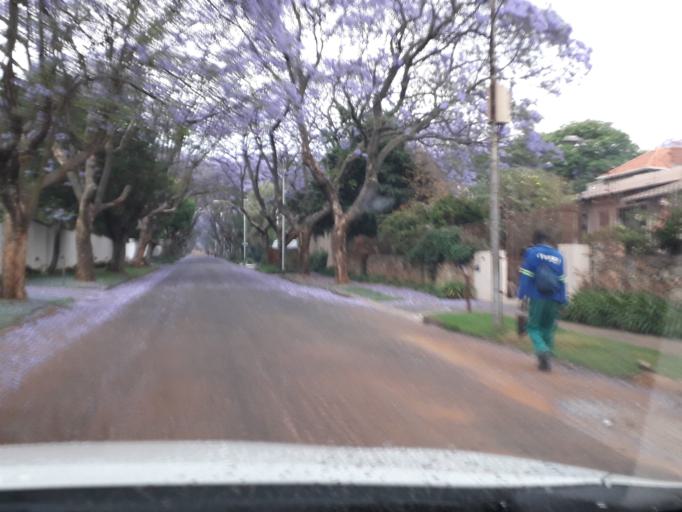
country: ZA
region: Gauteng
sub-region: City of Johannesburg Metropolitan Municipality
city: Johannesburg
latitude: -26.1412
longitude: 28.0484
